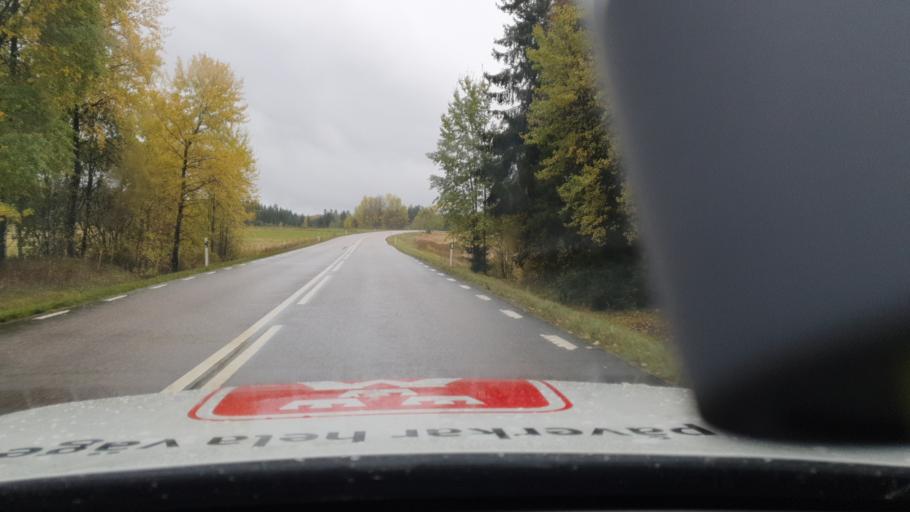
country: SE
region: Vaestra Goetaland
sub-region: Dals-Ed Kommun
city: Ed
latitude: 58.8838
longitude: 11.9055
